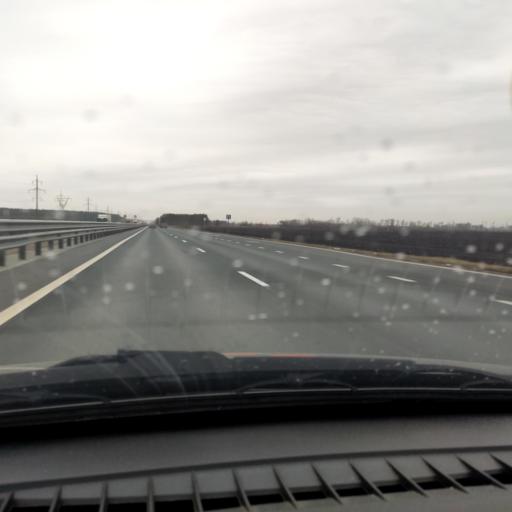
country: RU
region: Samara
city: Povolzhskiy
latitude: 53.5160
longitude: 49.6817
